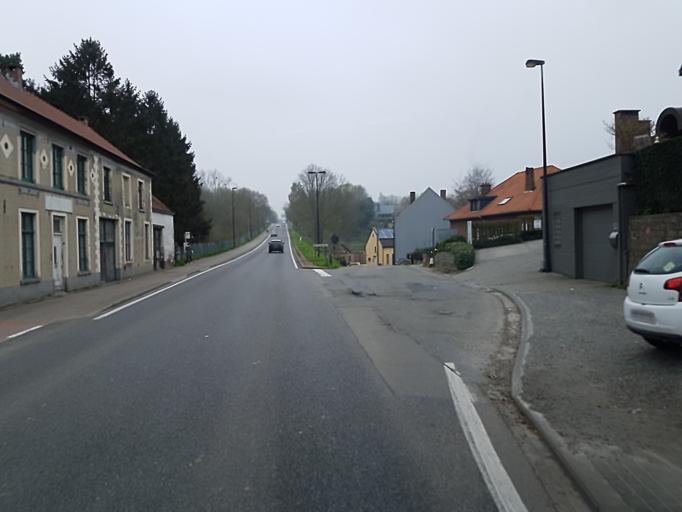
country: BE
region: Flanders
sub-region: Provincie Vlaams-Brabant
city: Beersel
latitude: 50.7293
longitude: 4.3070
